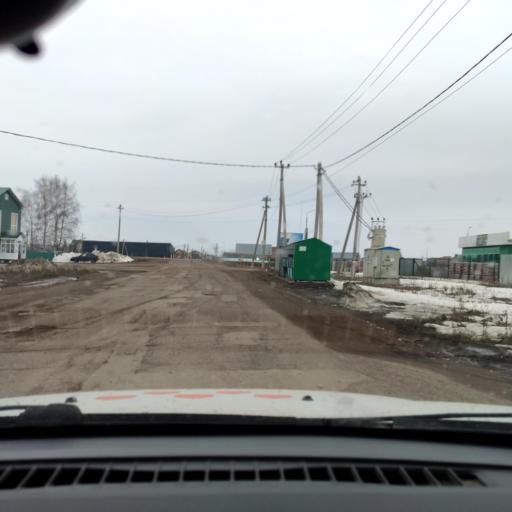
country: RU
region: Bashkortostan
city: Kushnarenkovo
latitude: 55.1063
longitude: 55.3310
